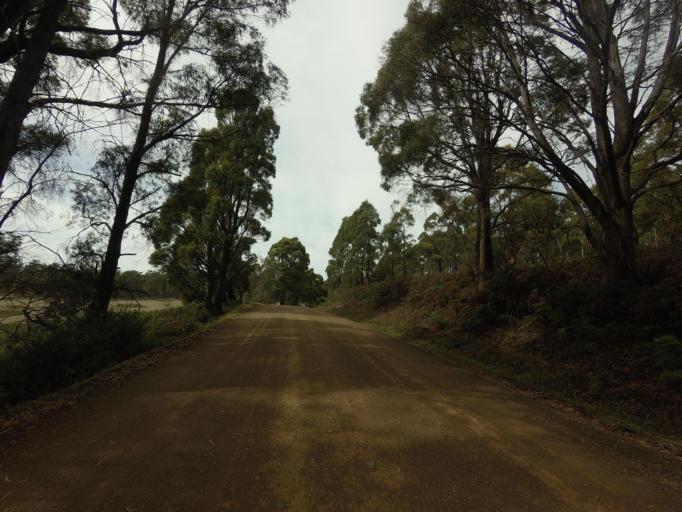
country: AU
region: Tasmania
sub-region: Sorell
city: Sorell
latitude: -42.4979
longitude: 147.6307
